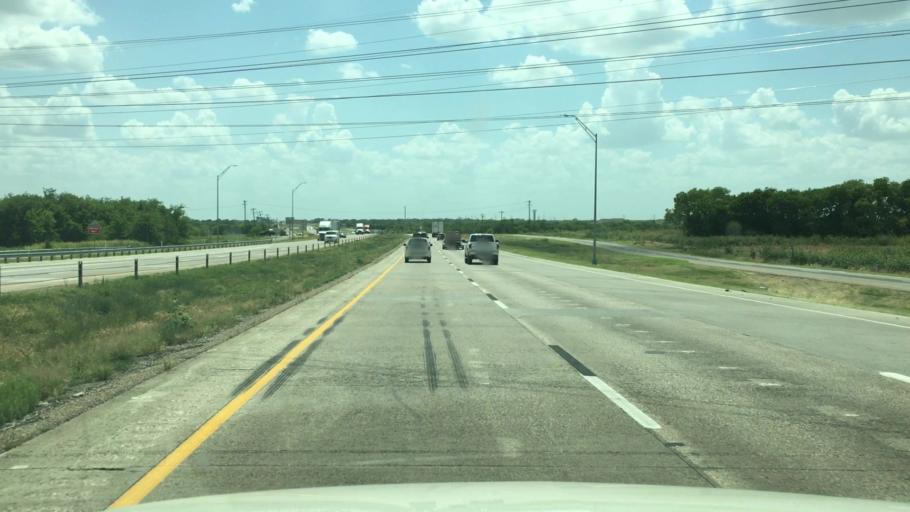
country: US
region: Texas
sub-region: Rockwall County
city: Royse City
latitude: 32.9581
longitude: -96.3508
